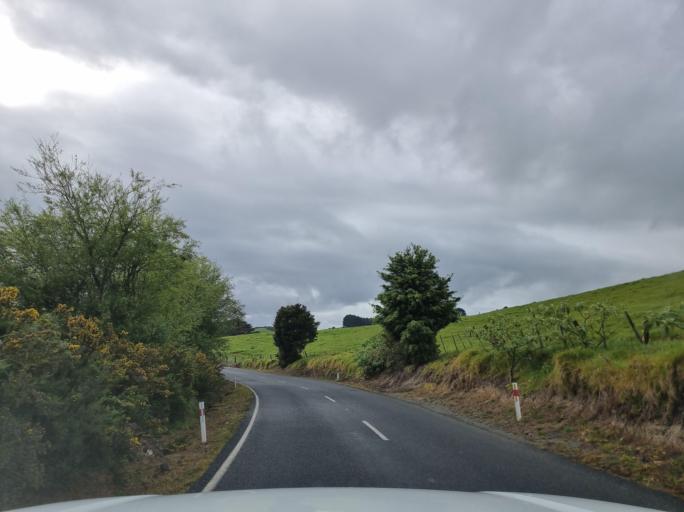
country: NZ
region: Northland
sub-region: Whangarei
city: Ruakaka
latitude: -35.9279
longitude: 174.4218
